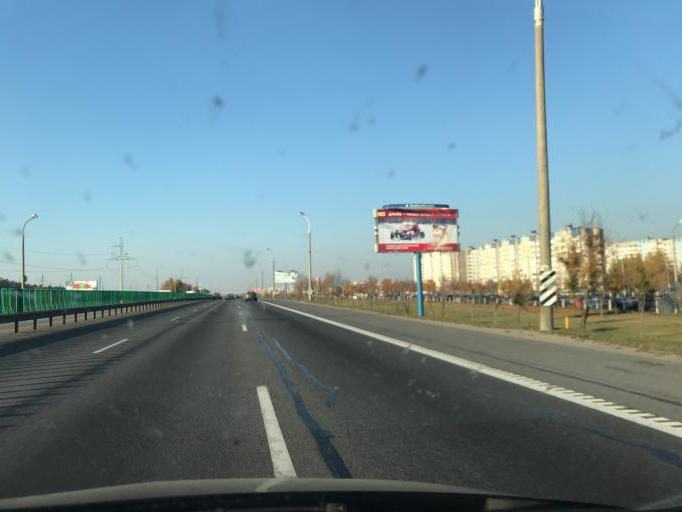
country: BY
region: Minsk
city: Malinovka
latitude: 53.8594
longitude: 27.4280
